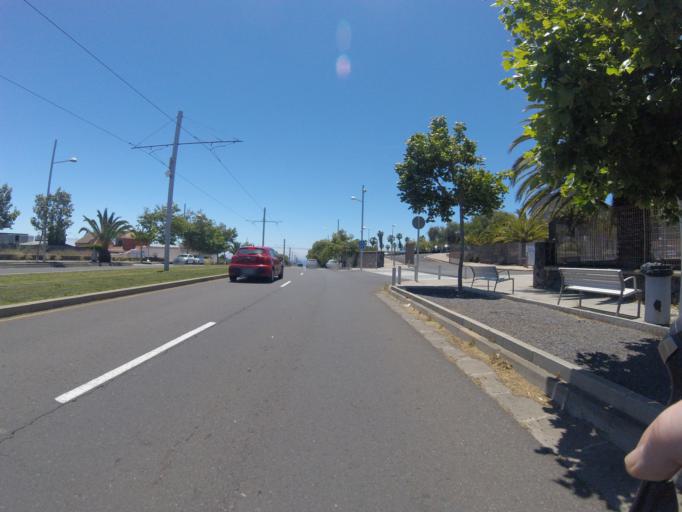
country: ES
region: Canary Islands
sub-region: Provincia de Santa Cruz de Tenerife
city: La Laguna
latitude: 28.4713
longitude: -16.3049
